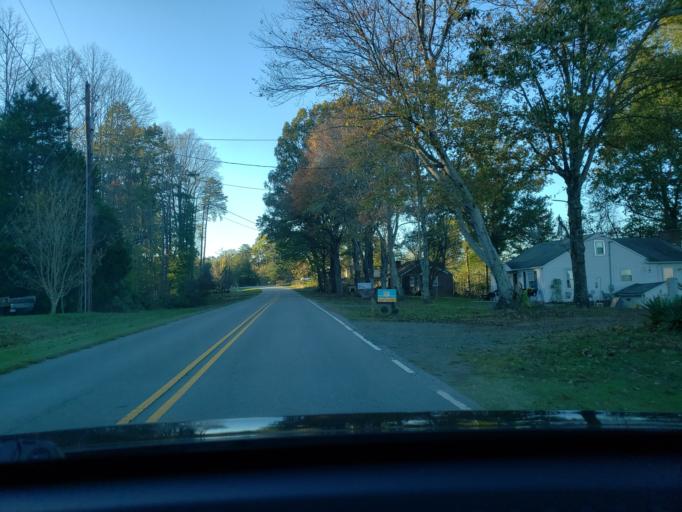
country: US
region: North Carolina
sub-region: Forsyth County
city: Walkertown
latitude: 36.2227
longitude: -80.1899
